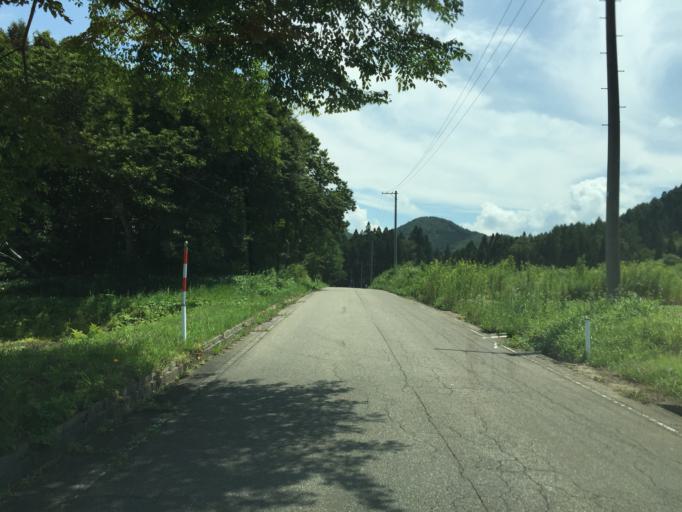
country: JP
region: Fukushima
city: Inawashiro
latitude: 37.5054
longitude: 140.0158
